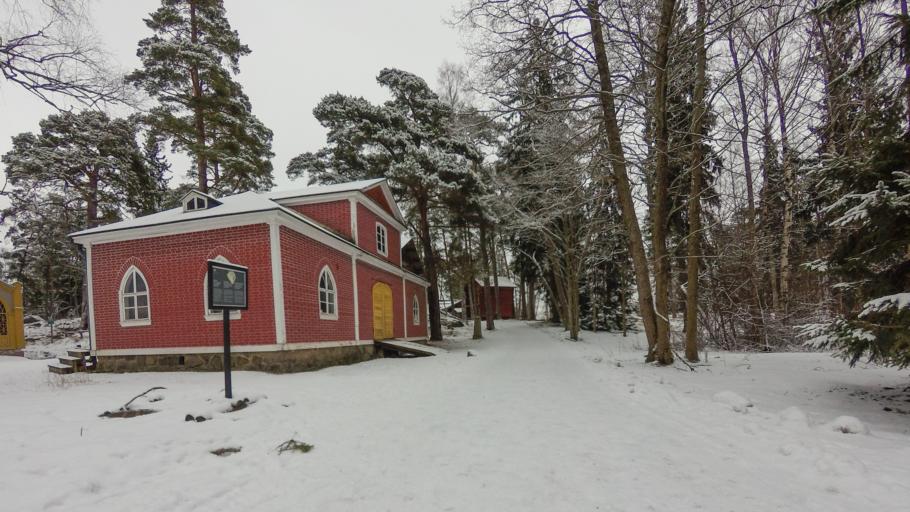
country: FI
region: Uusimaa
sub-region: Helsinki
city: Helsinki
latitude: 60.1809
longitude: 24.8859
